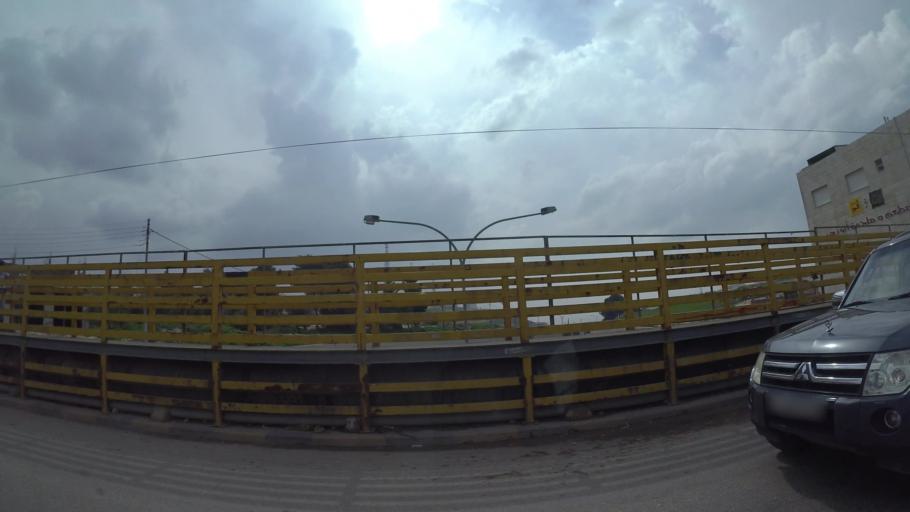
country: JO
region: Amman
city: Umm as Summaq
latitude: 31.8897
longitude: 35.8483
